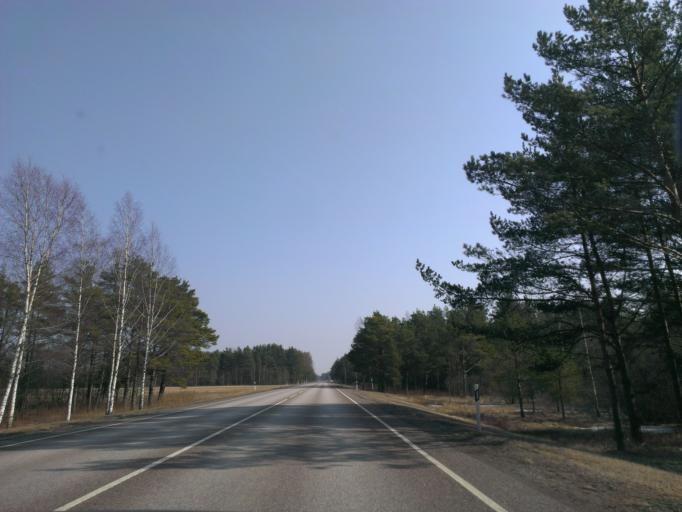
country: EE
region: Saare
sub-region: Orissaare vald
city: Orissaare
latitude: 58.5304
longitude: 22.9920
